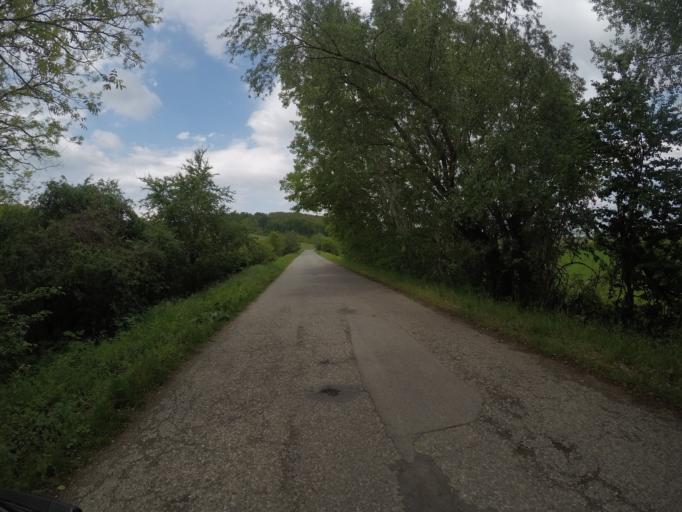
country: SK
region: Nitriansky
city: Sahy
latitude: 48.0872
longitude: 18.8681
